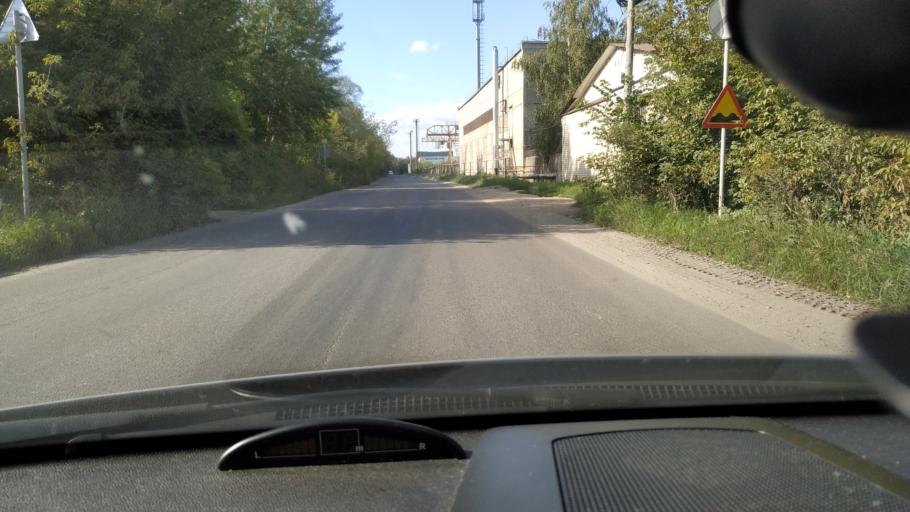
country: RU
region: Rjazan
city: Ryazan'
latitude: 54.6693
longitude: 39.6184
